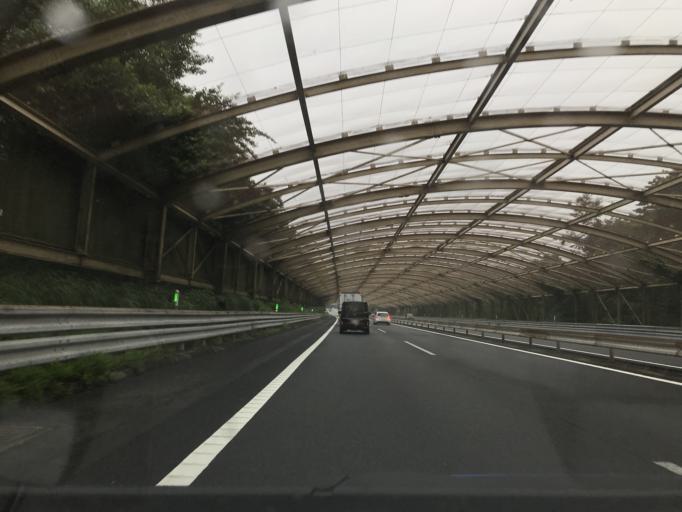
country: JP
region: Oita
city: Beppu
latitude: 33.3049
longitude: 131.4581
